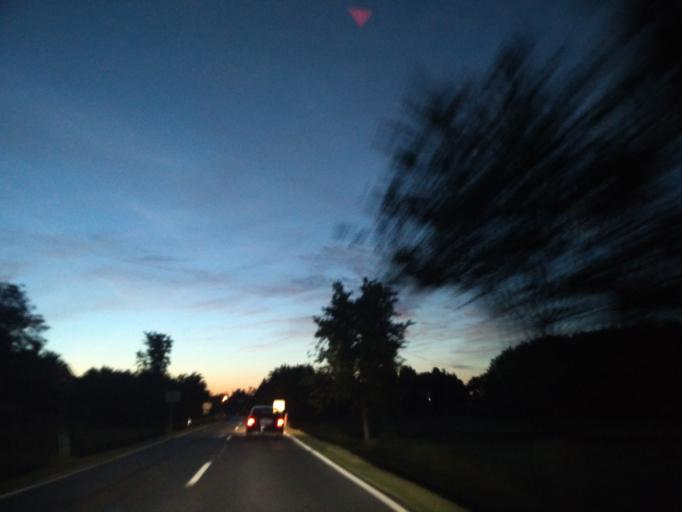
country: HU
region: Vas
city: Vasvar
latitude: 46.9777
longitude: 16.8421
